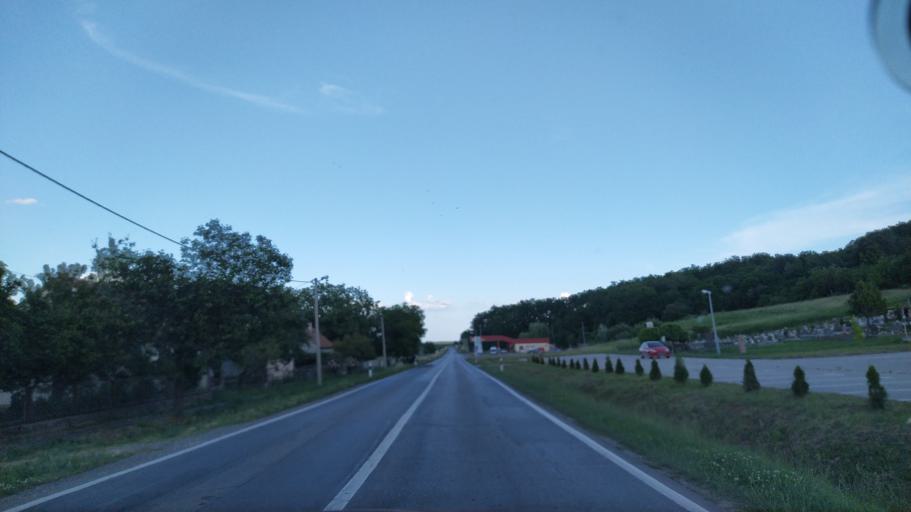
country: HR
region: Virovitick-Podravska
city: Suhopolje
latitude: 45.7494
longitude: 17.5876
